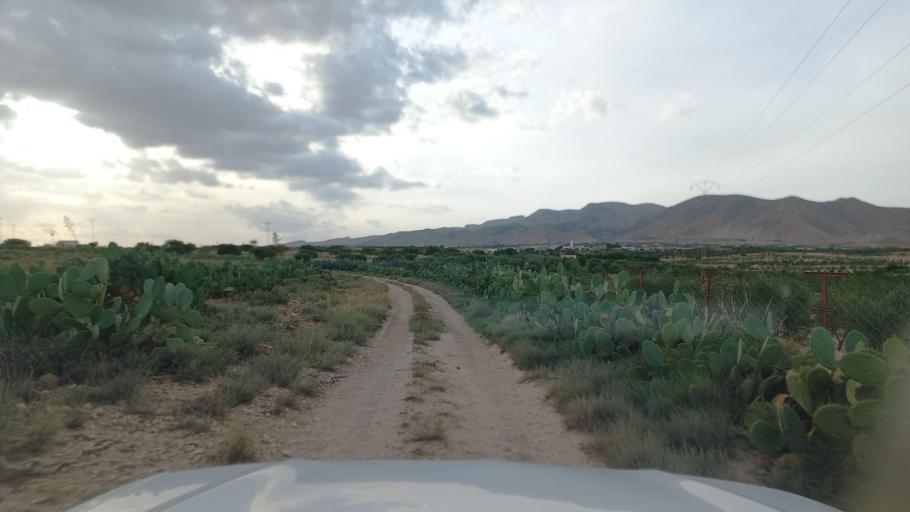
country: TN
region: Al Qasrayn
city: Sbiba
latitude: 35.4413
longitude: 9.0892
